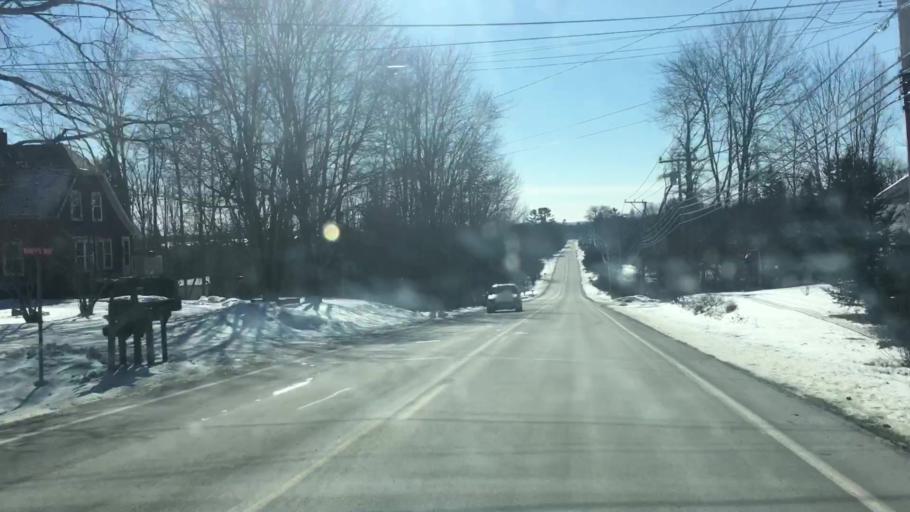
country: US
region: Maine
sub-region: Hancock County
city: Ellsworth
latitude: 44.5084
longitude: -68.4388
